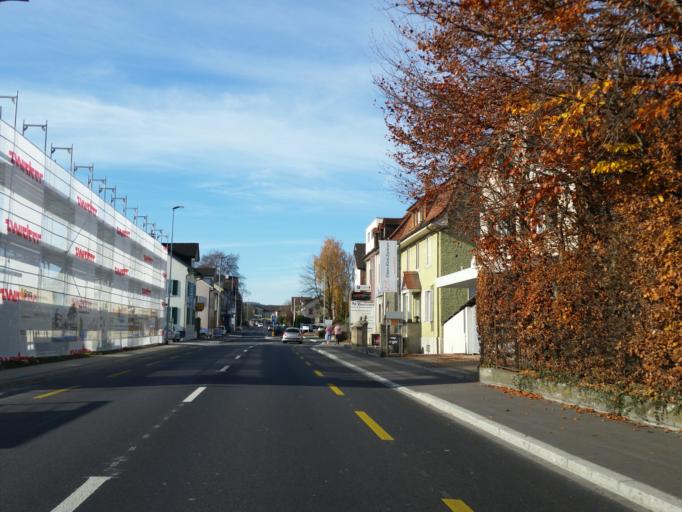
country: CH
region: Thurgau
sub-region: Arbon District
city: Amriswil
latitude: 47.5451
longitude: 9.2925
